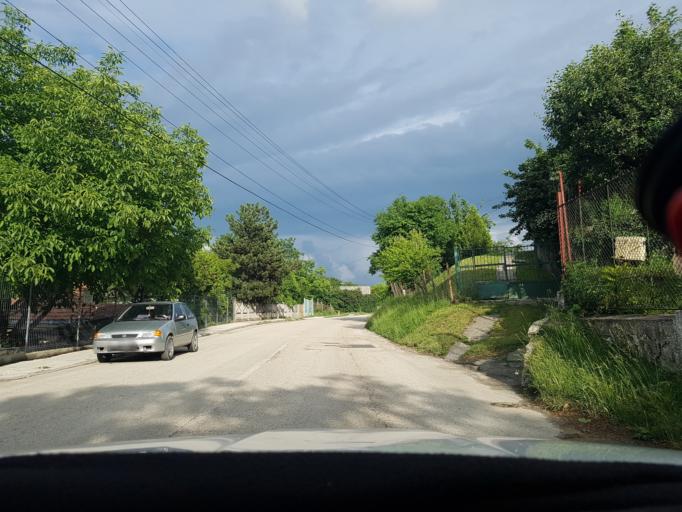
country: HU
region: Komarom-Esztergom
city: Labatlan
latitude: 47.7421
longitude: 18.5031
